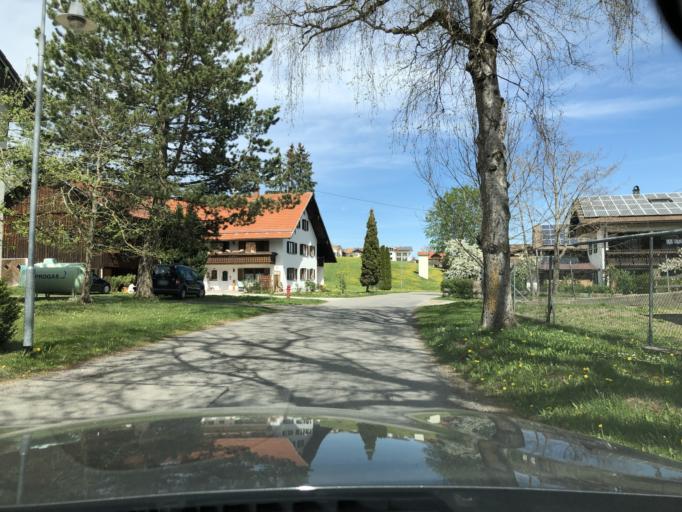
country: DE
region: Bavaria
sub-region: Swabia
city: Seeg
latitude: 47.6517
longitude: 10.6124
